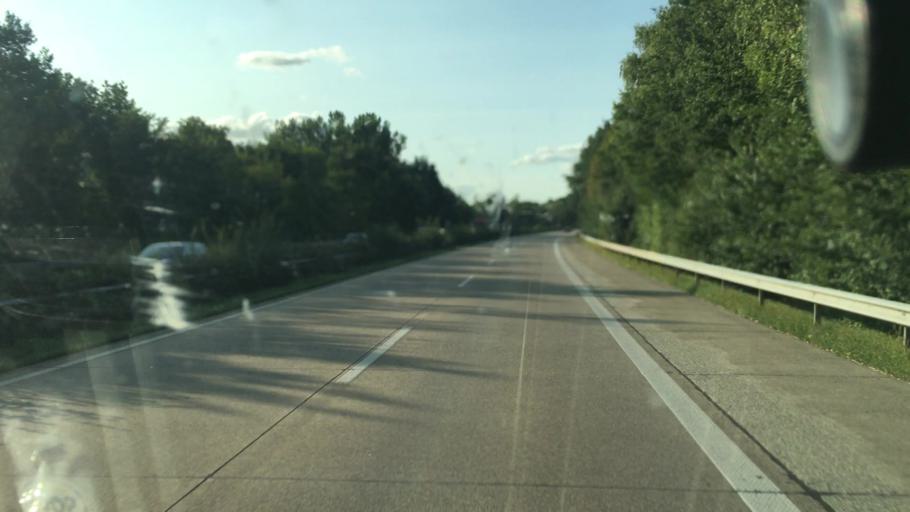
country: DE
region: Lower Saxony
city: Rastede
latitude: 53.2310
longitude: 8.1865
